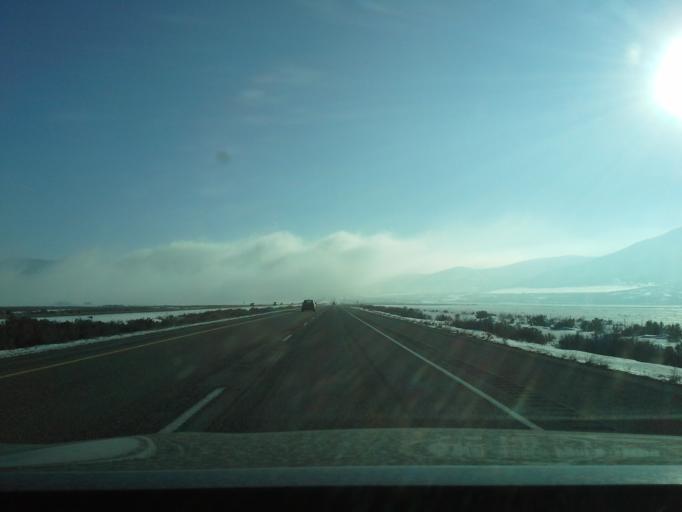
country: US
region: Idaho
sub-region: Oneida County
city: Malad City
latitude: 42.3943
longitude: -112.2005
